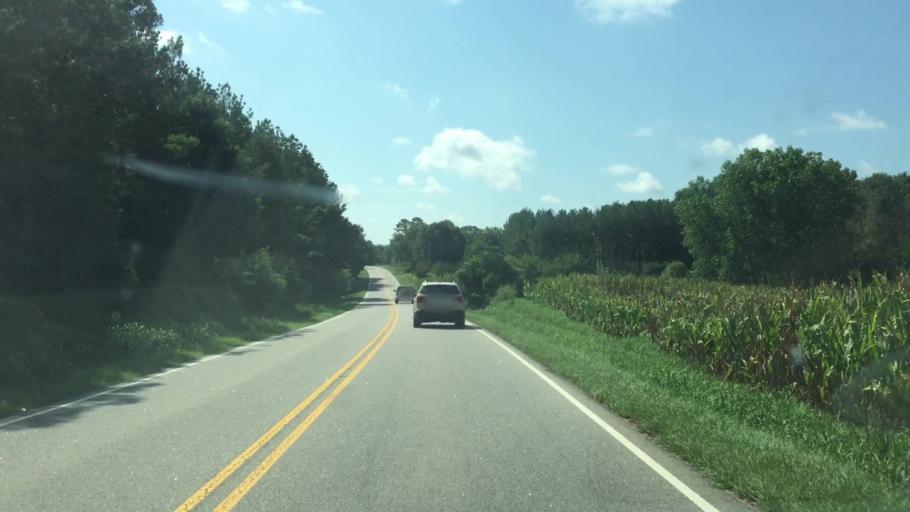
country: US
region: North Carolina
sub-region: Anson County
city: Burnsville
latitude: 35.0658
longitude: -80.2821
